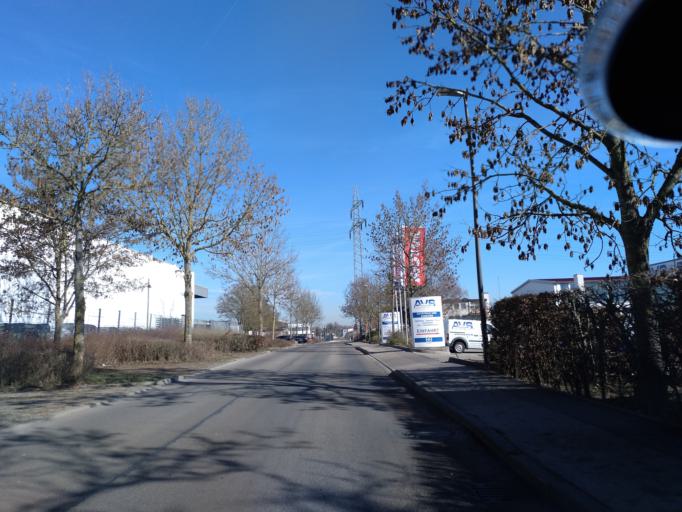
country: DE
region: Baden-Wuerttemberg
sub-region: Regierungsbezirk Stuttgart
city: Michelfeld
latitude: 49.1037
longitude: 9.7088
